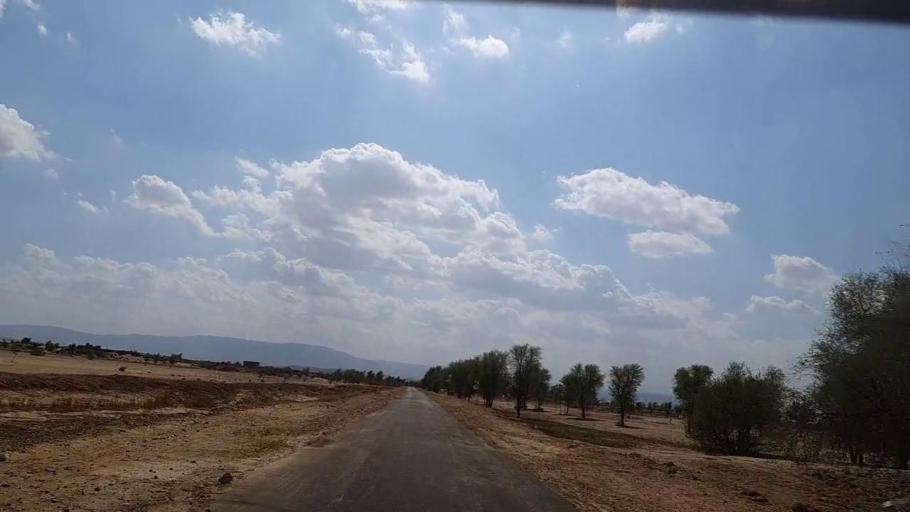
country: PK
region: Sindh
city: Johi
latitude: 26.5229
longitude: 67.4889
